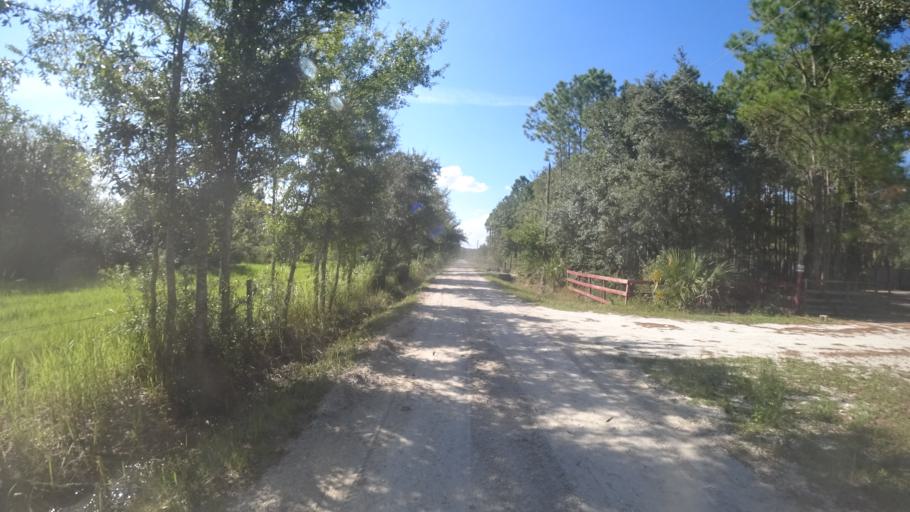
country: US
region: Florida
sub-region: Sarasota County
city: The Meadows
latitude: 27.4453
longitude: -82.2991
